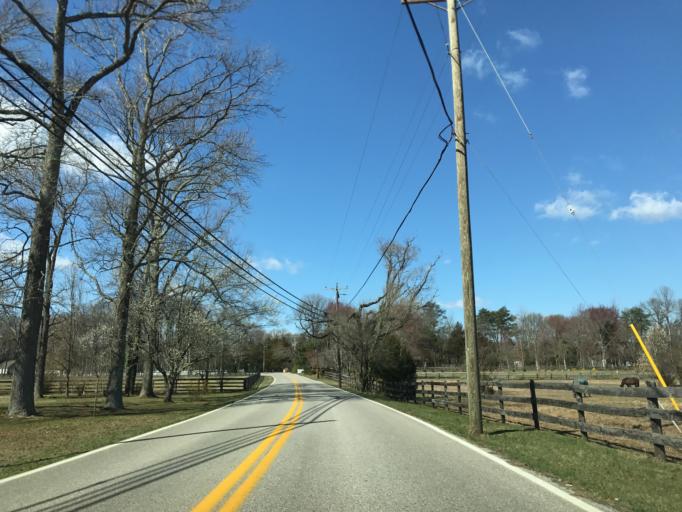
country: US
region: Maryland
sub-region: Anne Arundel County
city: Robinwood
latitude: 38.9532
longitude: -76.5186
